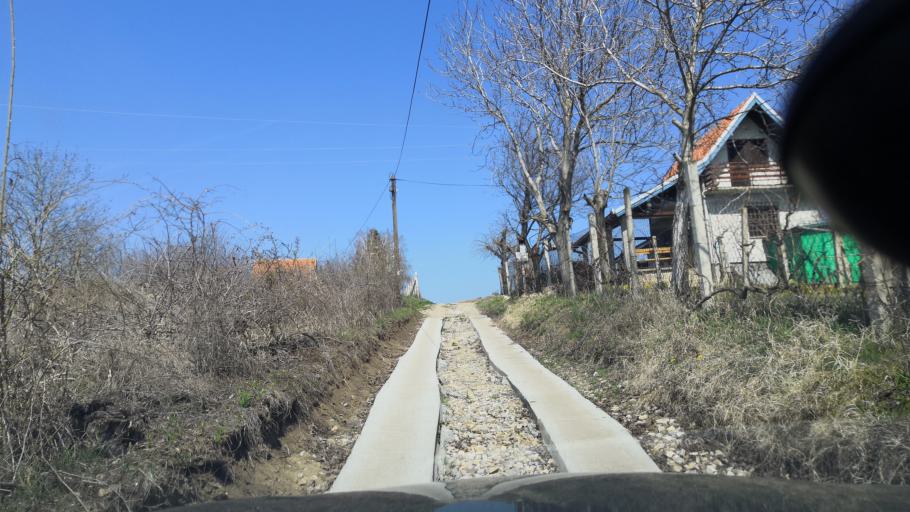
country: RS
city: Krcedin
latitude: 45.1610
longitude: 20.1866
